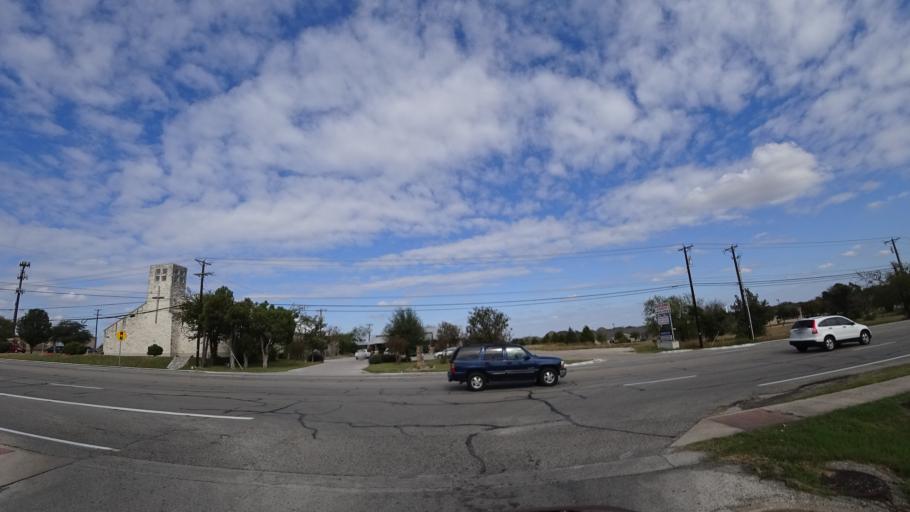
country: US
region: Texas
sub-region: Travis County
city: Pflugerville
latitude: 30.4439
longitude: -97.6299
